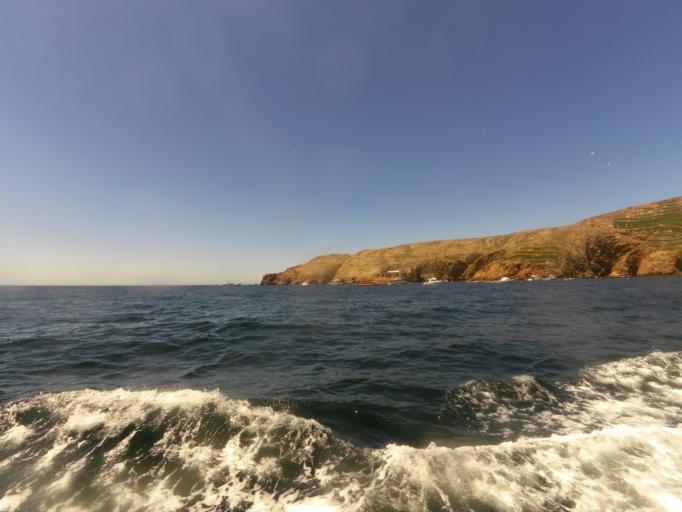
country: PT
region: Leiria
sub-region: Peniche
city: Peniche
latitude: 39.4122
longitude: -9.5044
